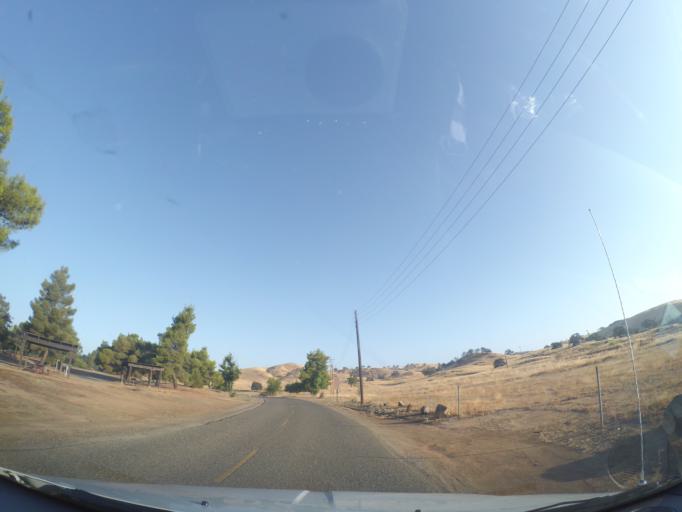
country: US
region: California
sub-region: Merced County
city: Planada
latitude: 37.5217
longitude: -120.3030
